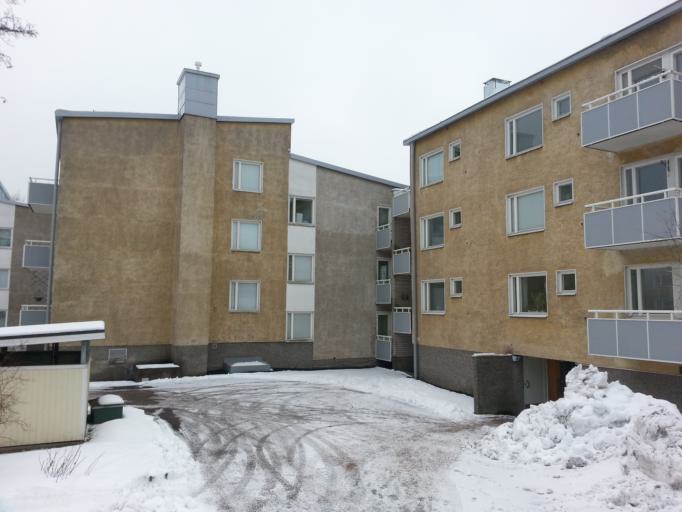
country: FI
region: Uusimaa
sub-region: Helsinki
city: Teekkarikylae
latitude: 60.2272
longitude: 24.8525
